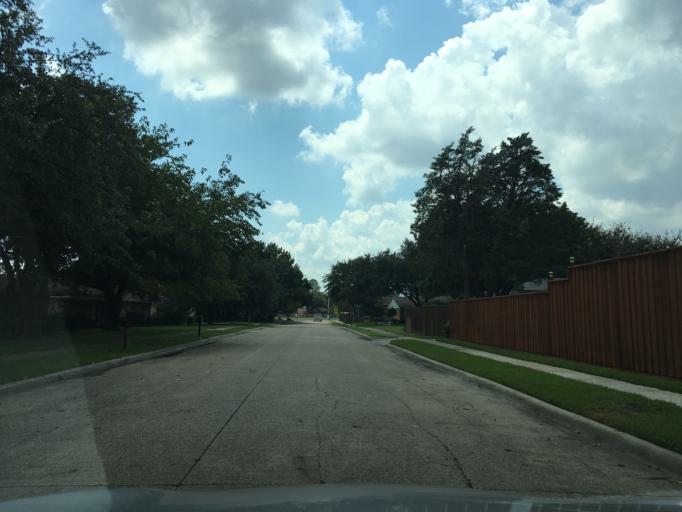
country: US
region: Texas
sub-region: Dallas County
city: Garland
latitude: 32.9364
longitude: -96.6466
